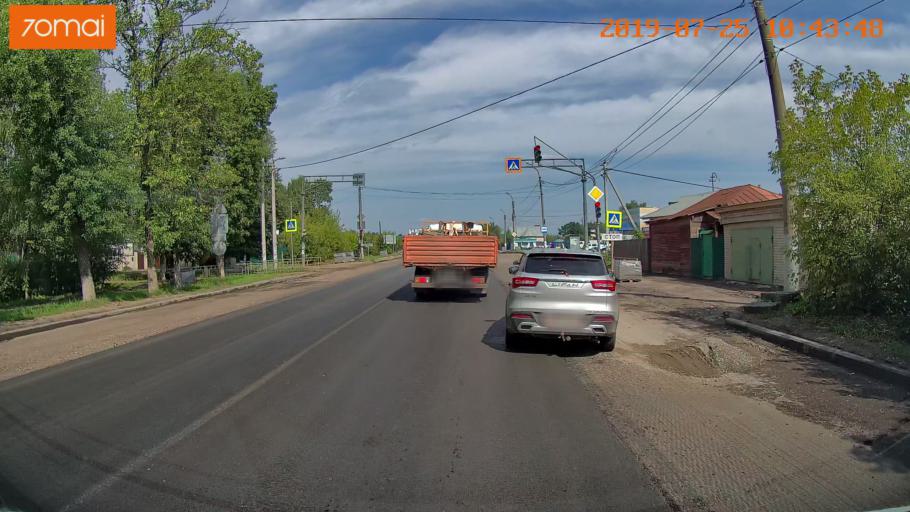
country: RU
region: Ivanovo
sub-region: Gorod Ivanovo
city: Ivanovo
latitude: 57.0382
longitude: 40.9686
